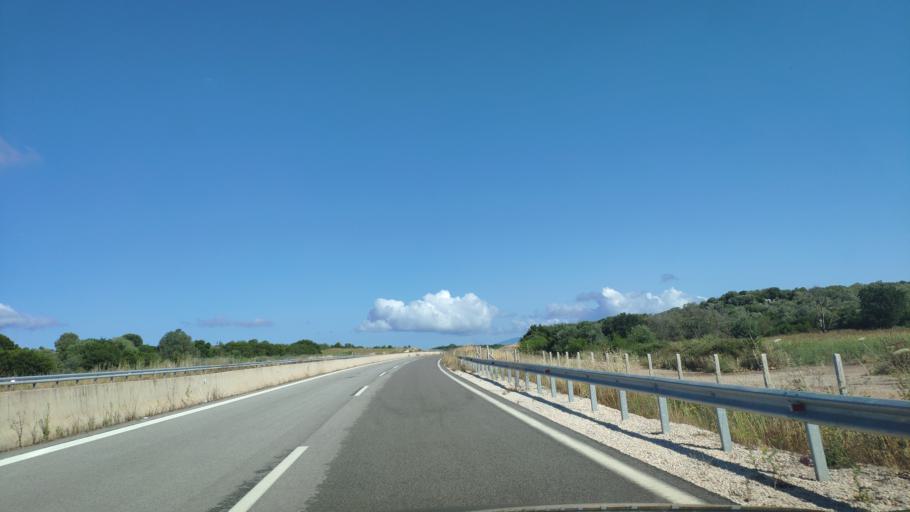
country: GR
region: West Greece
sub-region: Nomos Aitolias kai Akarnanias
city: Vonitsa
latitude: 38.9060
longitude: 20.8512
